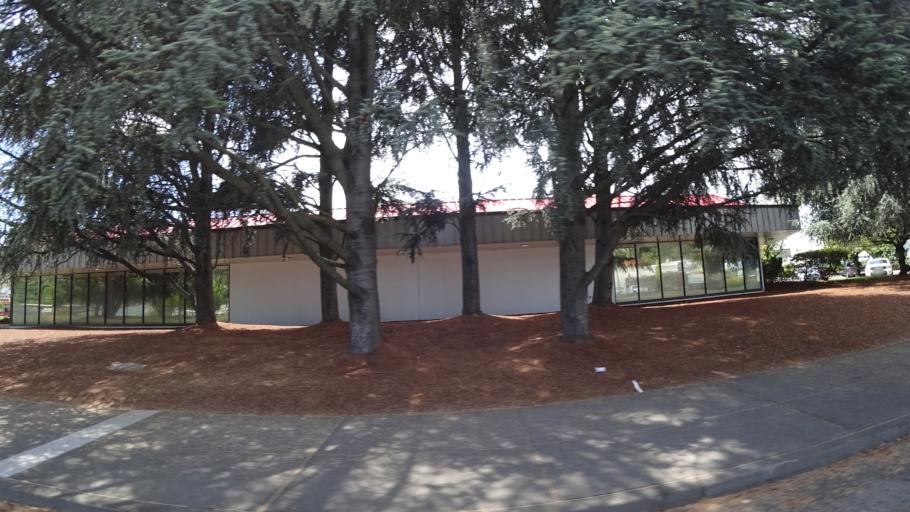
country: US
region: Oregon
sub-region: Multnomah County
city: Portland
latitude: 45.5568
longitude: -122.6985
